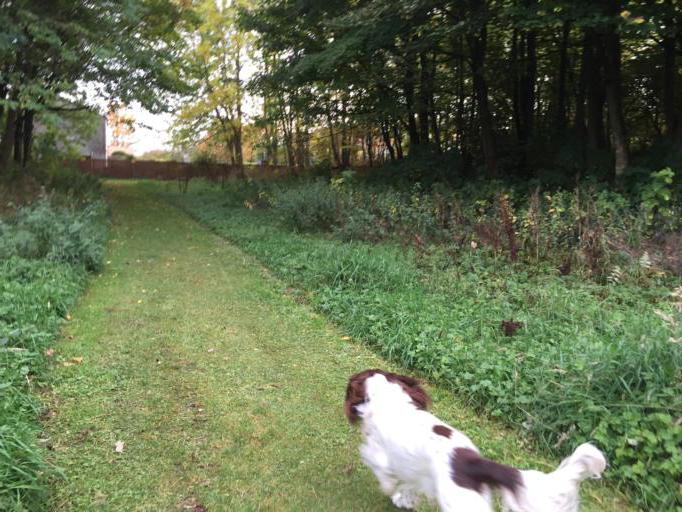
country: GB
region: Scotland
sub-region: West Lothian
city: Livingston
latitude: 55.9319
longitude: -3.5124
